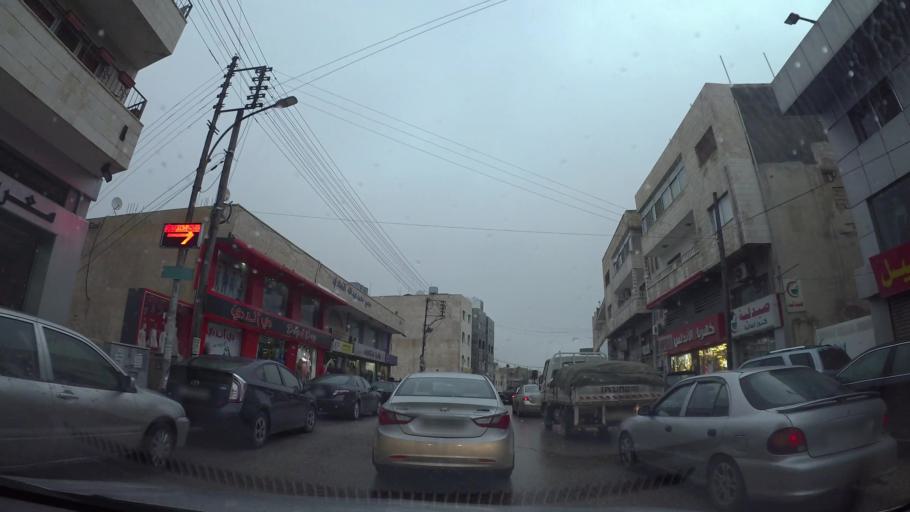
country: JO
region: Amman
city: Al Jubayhah
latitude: 32.0233
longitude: 35.8398
